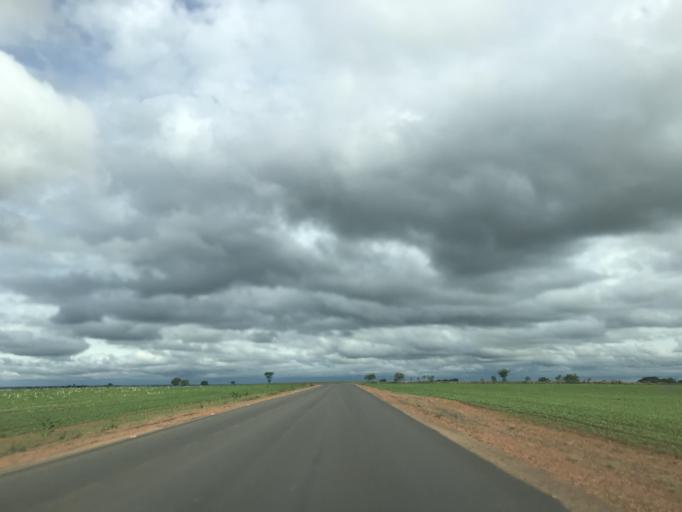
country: BR
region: Goias
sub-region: Vianopolis
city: Vianopolis
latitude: -16.9650
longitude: -48.6187
